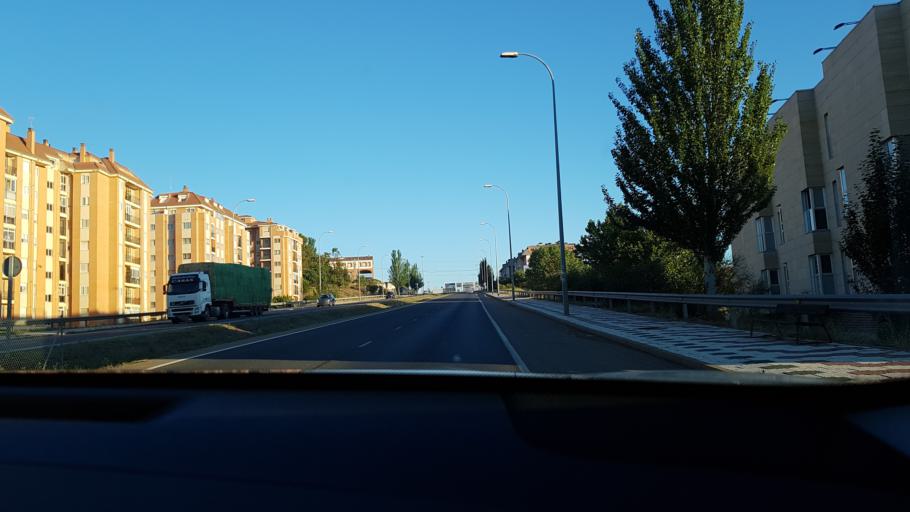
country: ES
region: Castille and Leon
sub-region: Provincia de Zamora
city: Zamora
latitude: 41.5166
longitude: -5.7470
